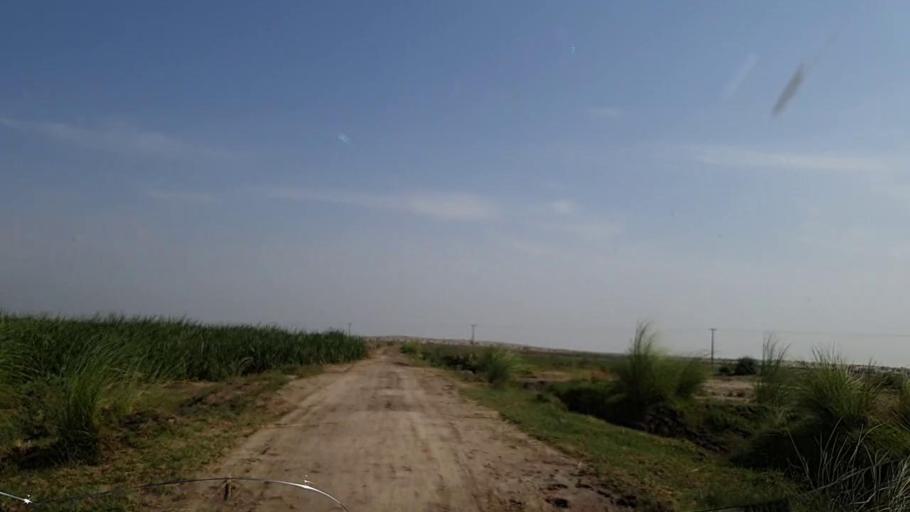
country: PK
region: Sindh
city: Khanpur
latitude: 27.6864
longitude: 69.3678
